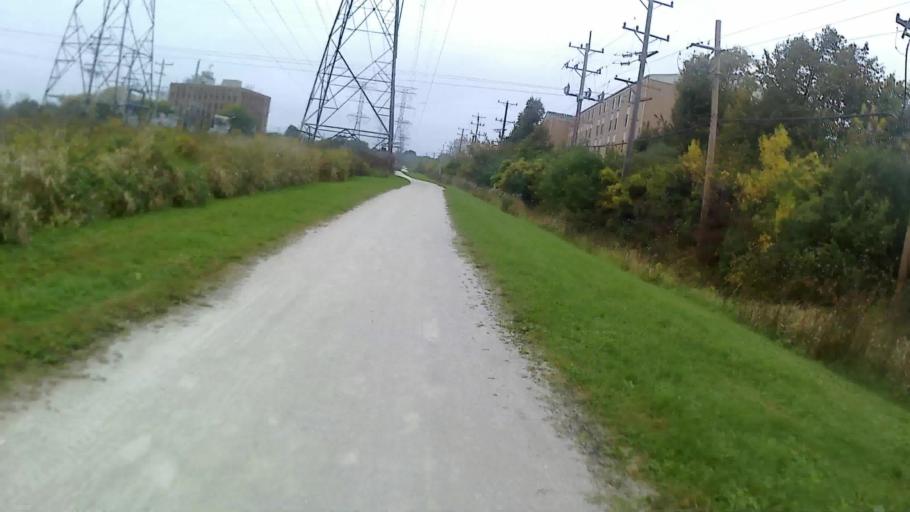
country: US
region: Illinois
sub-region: Kane County
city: Aurora
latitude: 41.7880
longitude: -88.2809
